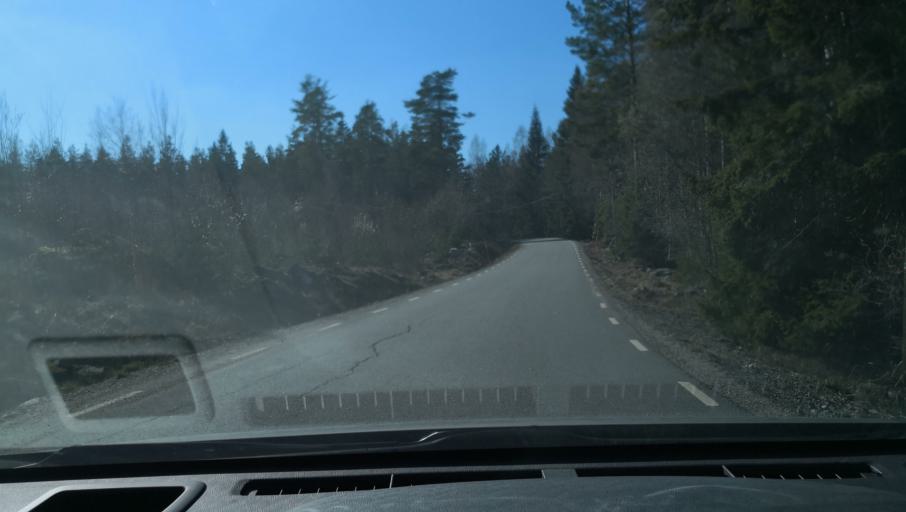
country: SE
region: Vaestmanland
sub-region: Sala Kommun
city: Sala
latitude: 59.9287
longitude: 16.4571
